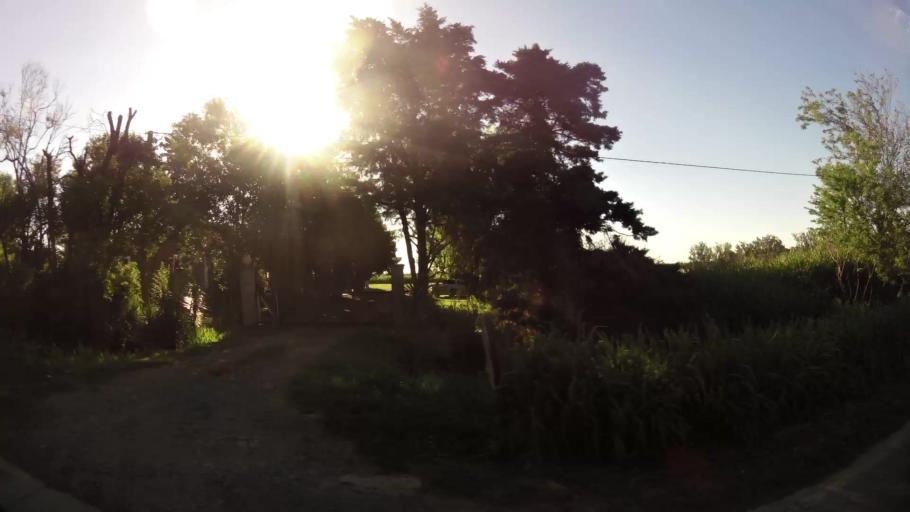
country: AR
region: Cordoba
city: San Francisco
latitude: -31.4494
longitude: -62.1017
